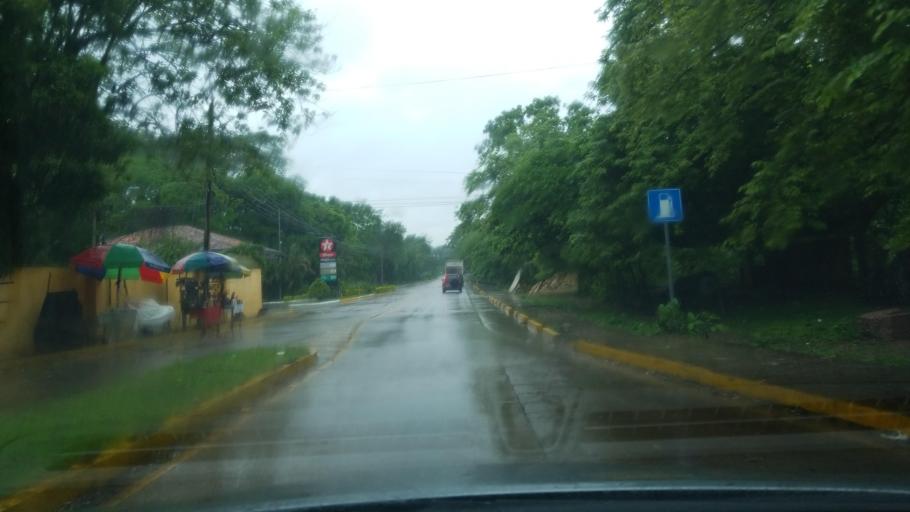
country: HN
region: Copan
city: Copan
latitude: 14.8398
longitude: -89.1471
